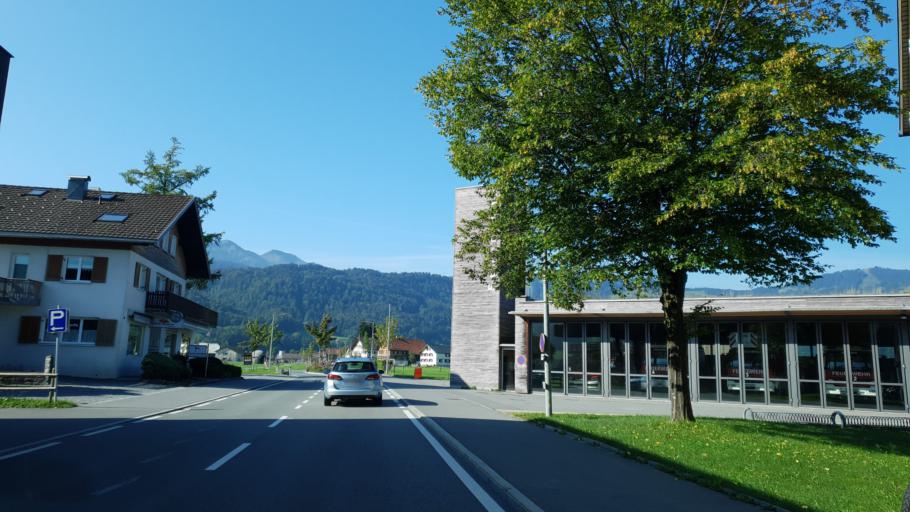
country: AT
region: Vorarlberg
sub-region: Politischer Bezirk Bregenz
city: Andelsbuch
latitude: 47.4111
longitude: 9.8927
